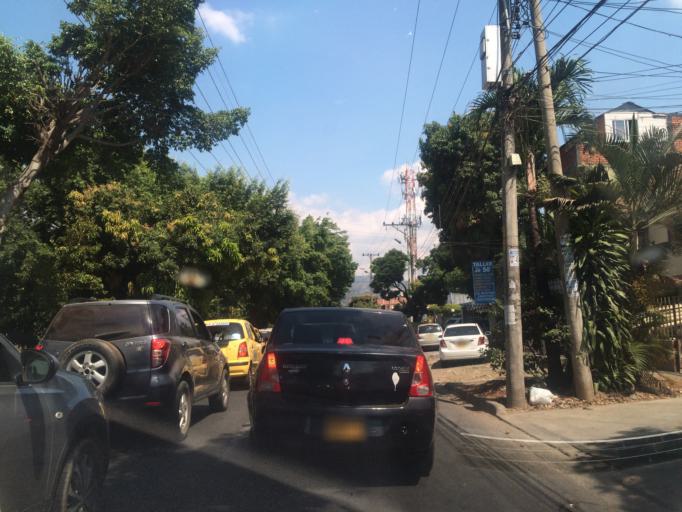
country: CO
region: Valle del Cauca
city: Cali
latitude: 3.4088
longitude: -76.5337
